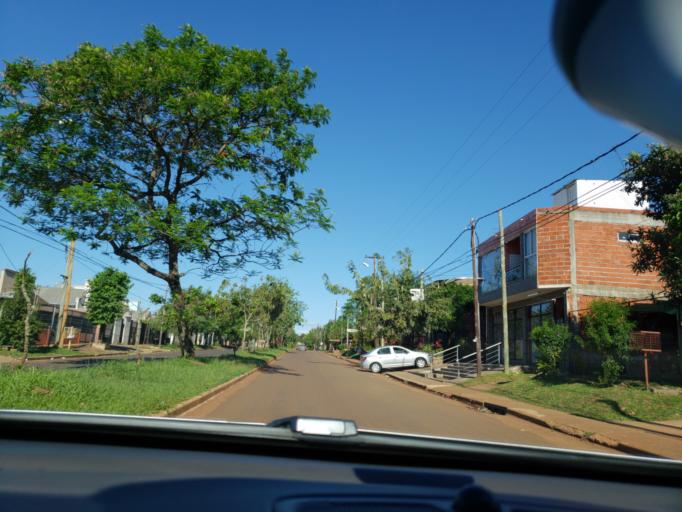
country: AR
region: Misiones
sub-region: Departamento de Capital
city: Posadas
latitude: -27.3849
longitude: -55.9256
